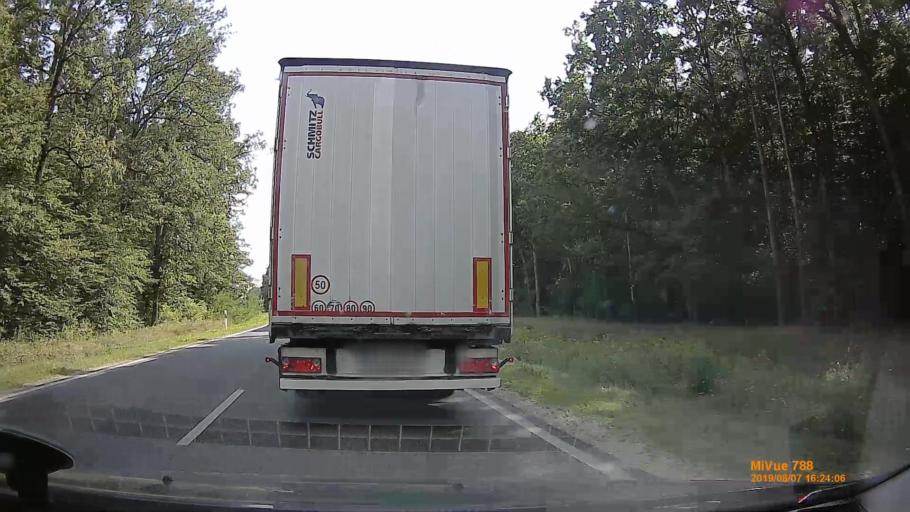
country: HU
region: Zala
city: Zalalovo
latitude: 46.7402
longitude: 16.5543
